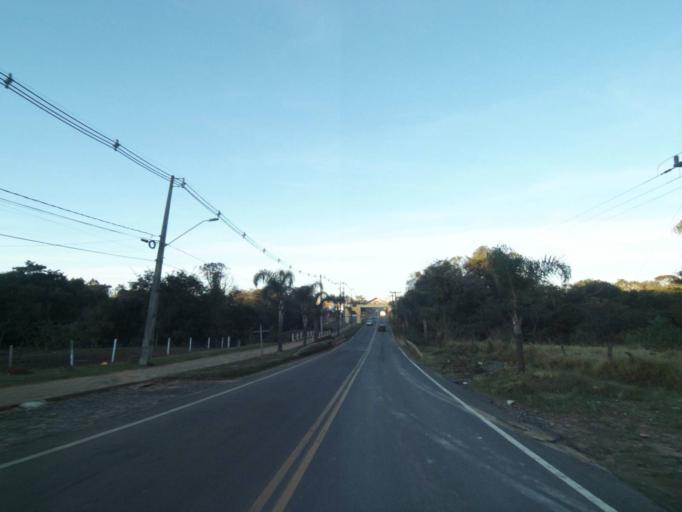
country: BR
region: Parana
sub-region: Tibagi
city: Tibagi
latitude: -24.5117
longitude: -50.4216
